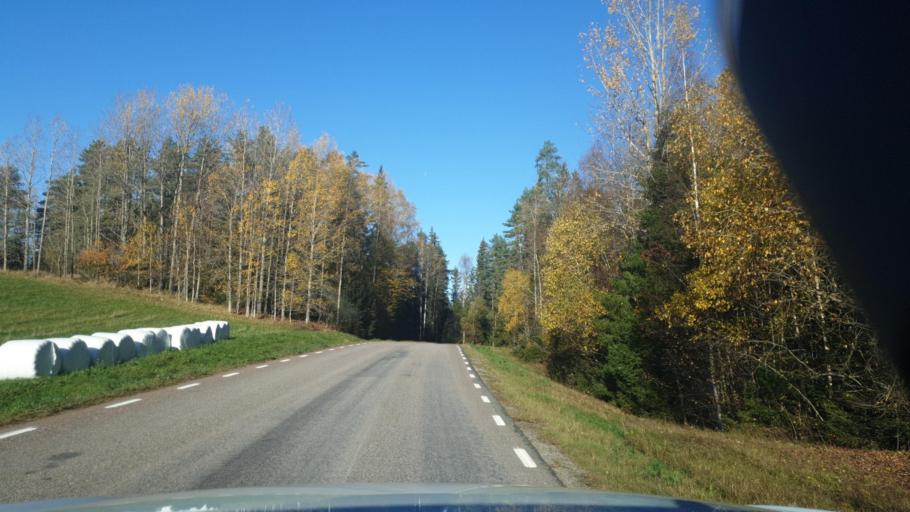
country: SE
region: Vaermland
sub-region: Arvika Kommun
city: Arvika
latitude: 59.6051
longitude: 12.7603
